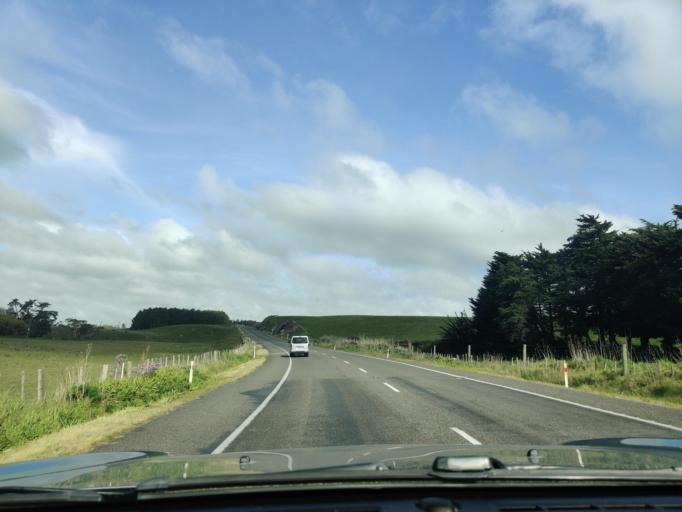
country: NZ
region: Manawatu-Wanganui
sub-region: Rangitikei District
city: Bulls
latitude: -40.0703
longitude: 175.2284
